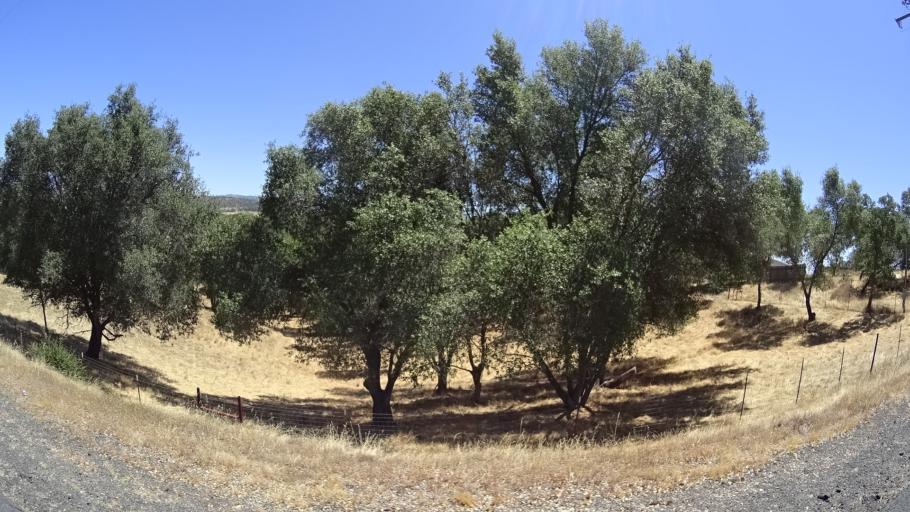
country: US
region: California
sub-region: Calaveras County
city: Copperopolis
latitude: 37.9841
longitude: -120.6915
